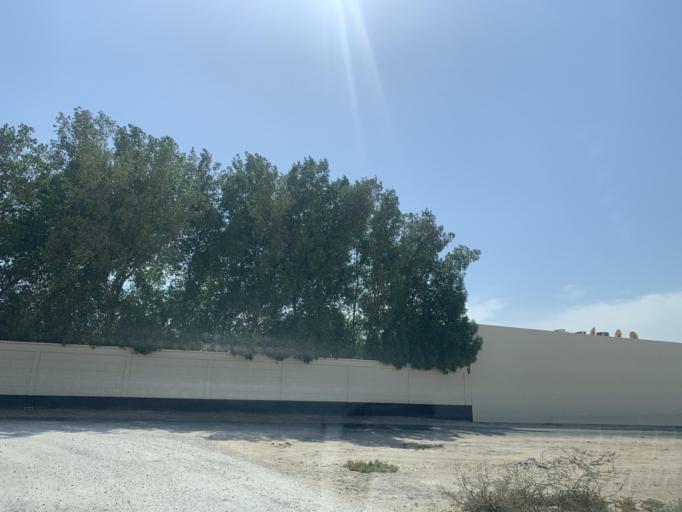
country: BH
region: Northern
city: Madinat `Isa
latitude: 26.1845
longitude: 50.4717
